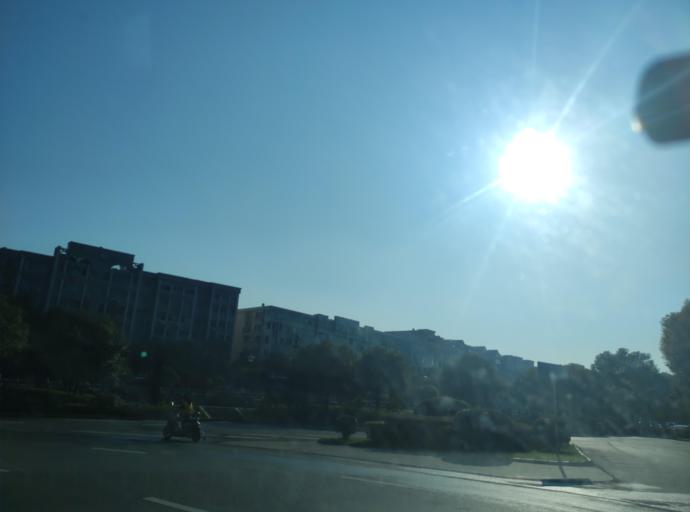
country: CN
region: Jiangxi Sheng
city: Pingxiang
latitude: 27.6287
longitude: 113.8510
